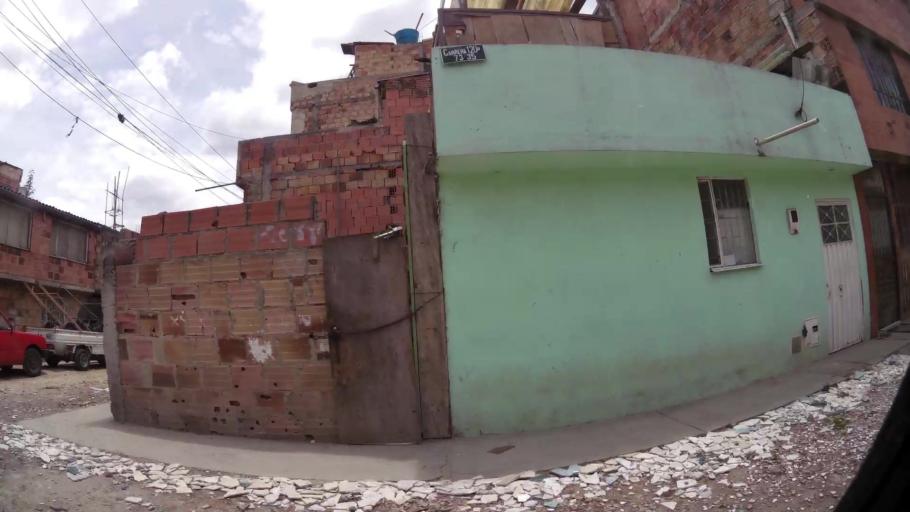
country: CO
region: Cundinamarca
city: Funza
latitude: 4.7187
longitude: -74.1327
